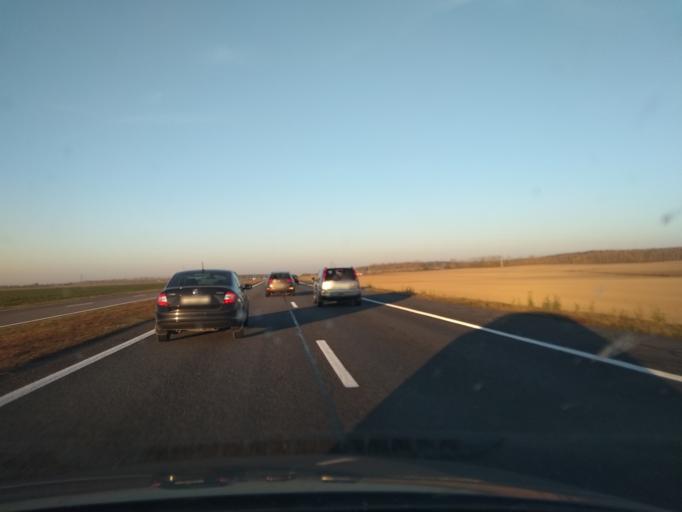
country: BY
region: Brest
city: Baranovichi
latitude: 53.2252
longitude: 26.1595
